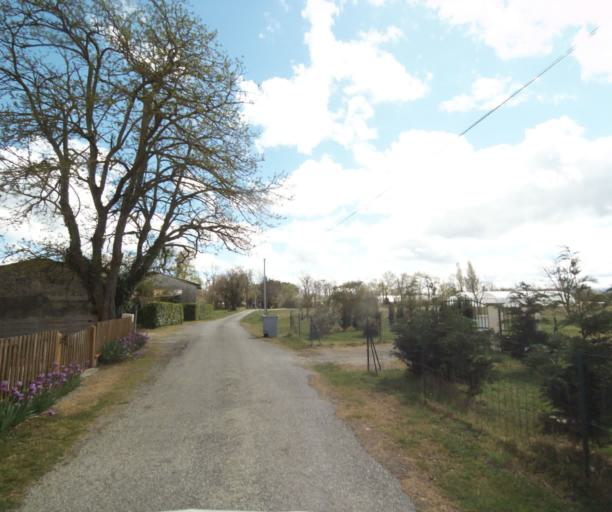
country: FR
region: Midi-Pyrenees
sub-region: Departement de l'Ariege
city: Saverdun
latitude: 43.2616
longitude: 1.5968
